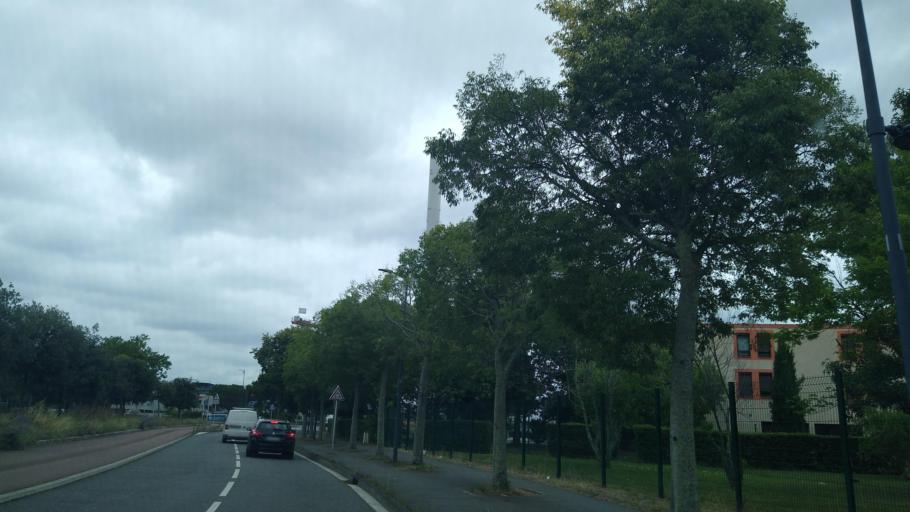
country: FR
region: Midi-Pyrenees
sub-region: Departement de la Haute-Garonne
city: Portet-sur-Garonne
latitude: 43.5698
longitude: 1.3890
